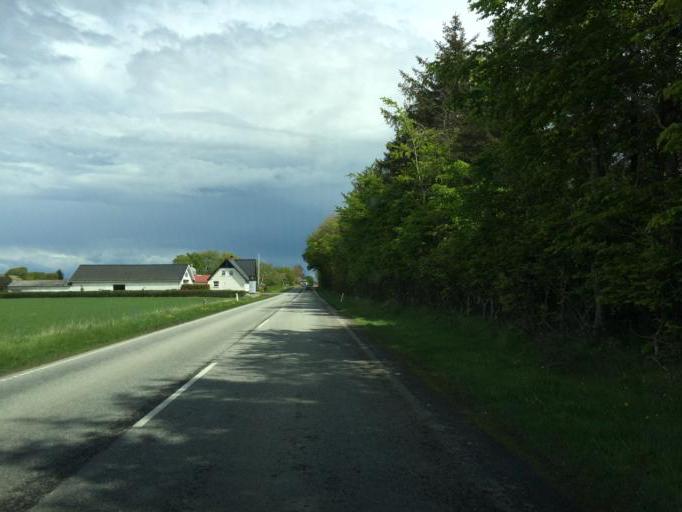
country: DK
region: North Denmark
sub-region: Vesthimmerland Kommune
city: Farso
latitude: 56.8376
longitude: 9.4147
